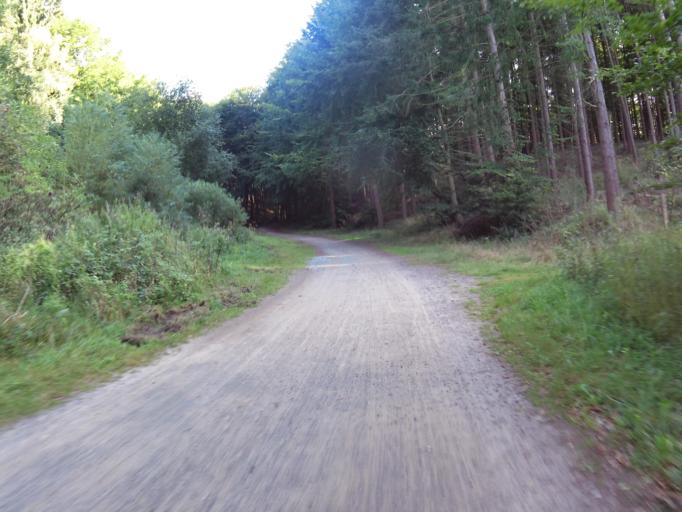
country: DE
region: Mecklenburg-Vorpommern
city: Seebad Bansin
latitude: 53.9875
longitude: 14.1167
